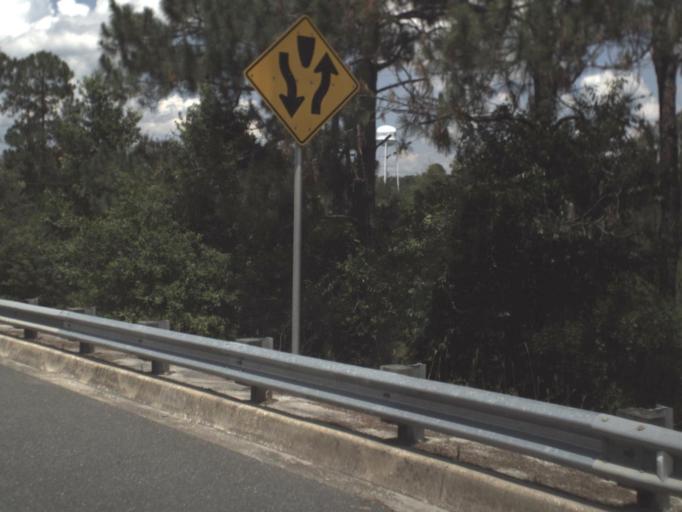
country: US
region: Florida
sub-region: Baker County
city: Macclenny
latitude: 30.2596
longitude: -82.1229
